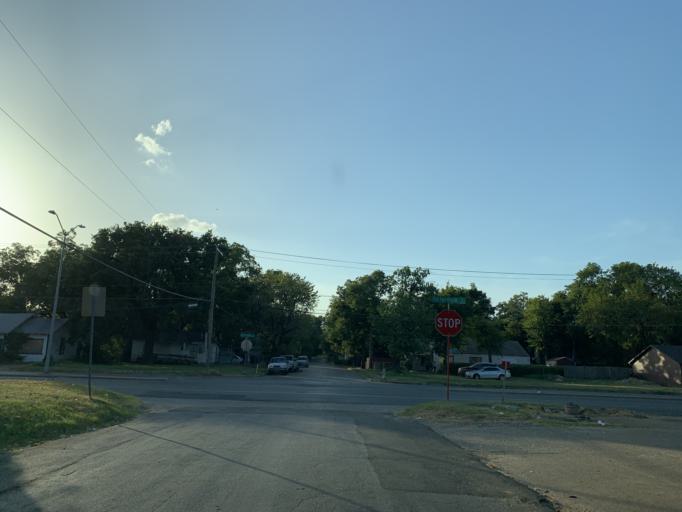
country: US
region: Texas
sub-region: Dallas County
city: Dallas
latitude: 32.7641
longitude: -96.7429
